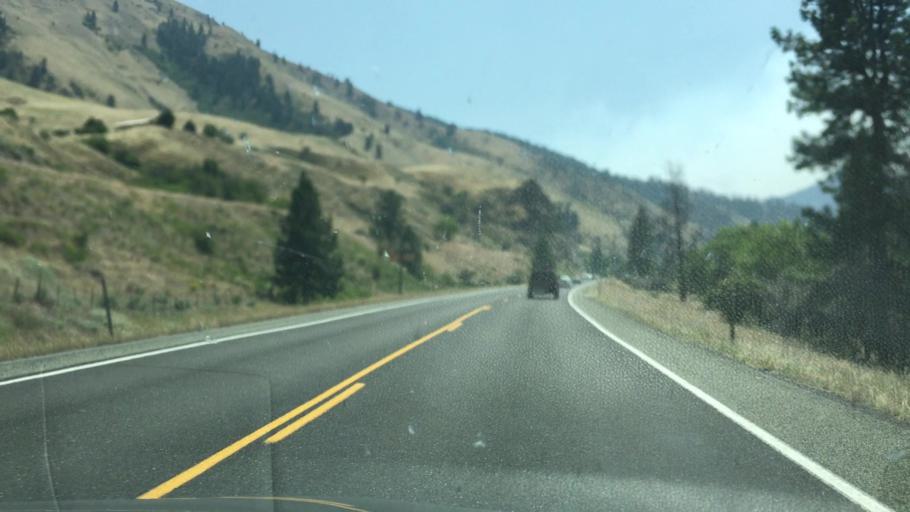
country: US
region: Idaho
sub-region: Valley County
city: McCall
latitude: 45.3383
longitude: -116.3478
